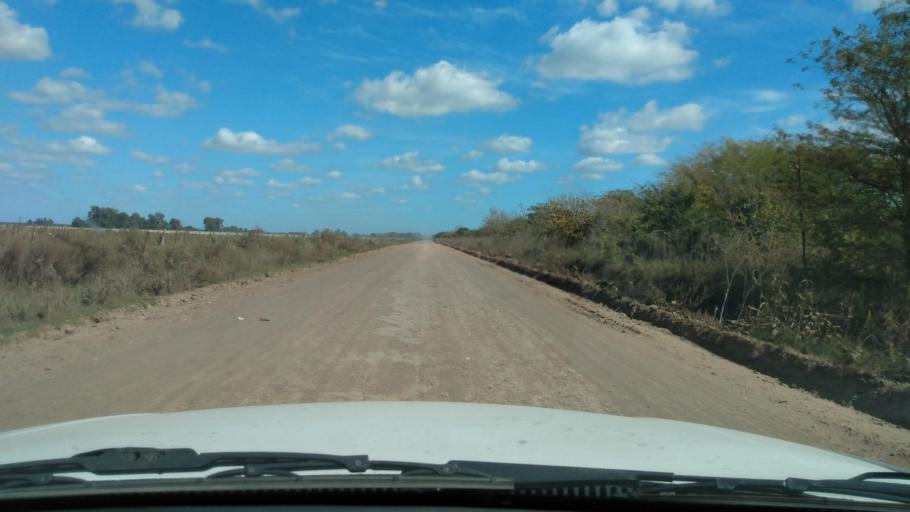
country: AR
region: Buenos Aires
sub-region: Partido de Navarro
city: Navarro
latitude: -35.0256
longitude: -59.4402
